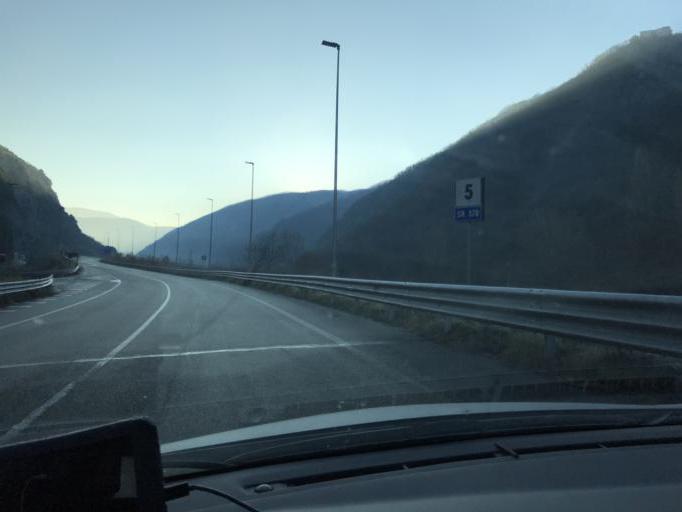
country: IT
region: Latium
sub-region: Provincia di Rieti
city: Cittaducale
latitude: 42.3586
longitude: 12.9308
